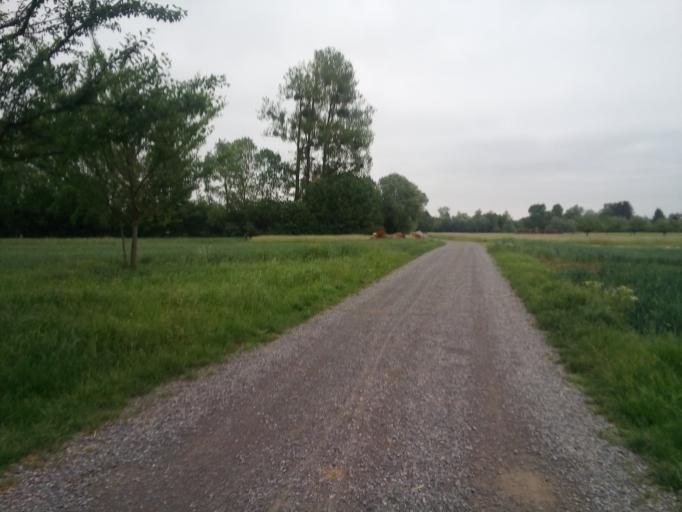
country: DE
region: Baden-Wuerttemberg
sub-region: Karlsruhe Region
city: Lichtenau
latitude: 48.7320
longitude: 7.9994
